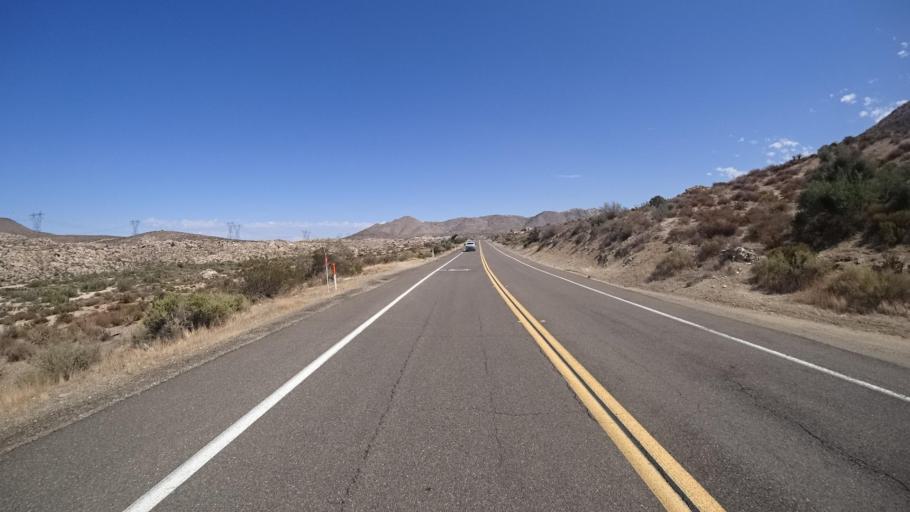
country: MX
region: Baja California
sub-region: Tecate
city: Cereso del Hongo
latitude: 32.6256
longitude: -116.1474
